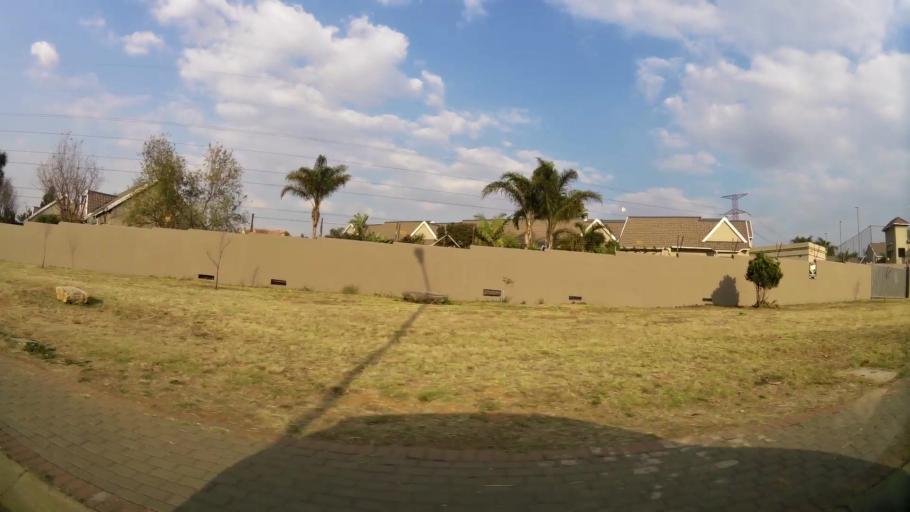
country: ZA
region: Gauteng
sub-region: City of Johannesburg Metropolitan Municipality
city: Modderfontein
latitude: -26.1337
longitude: 28.1831
